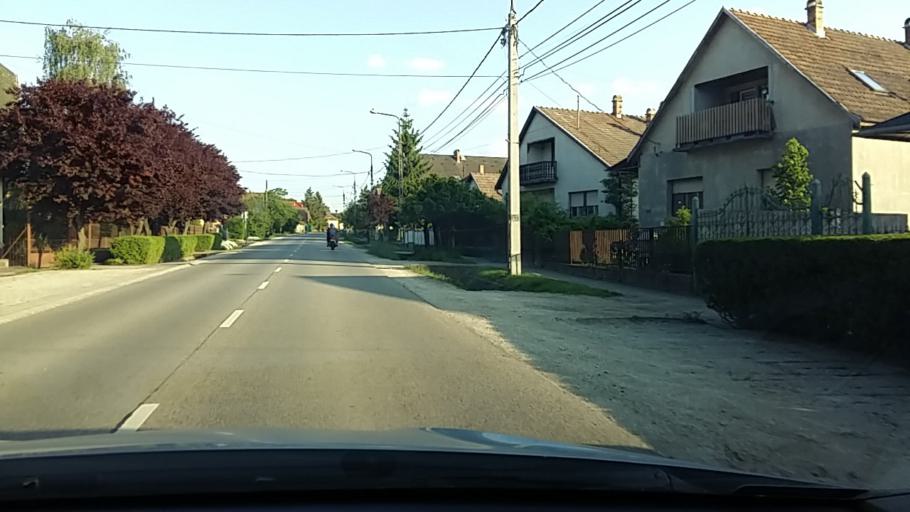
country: HU
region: Pest
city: Orbottyan
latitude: 47.7134
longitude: 19.2342
